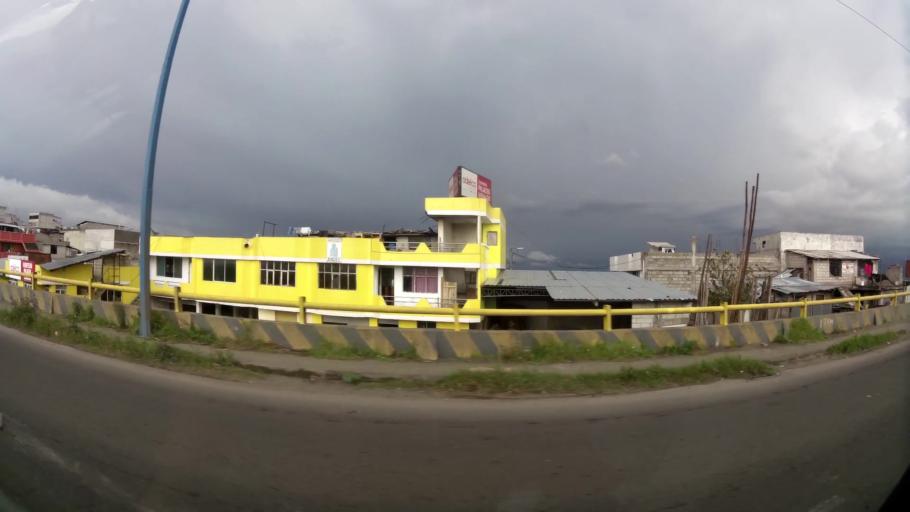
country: EC
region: Pichincha
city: Quito
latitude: -0.3042
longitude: -78.5215
